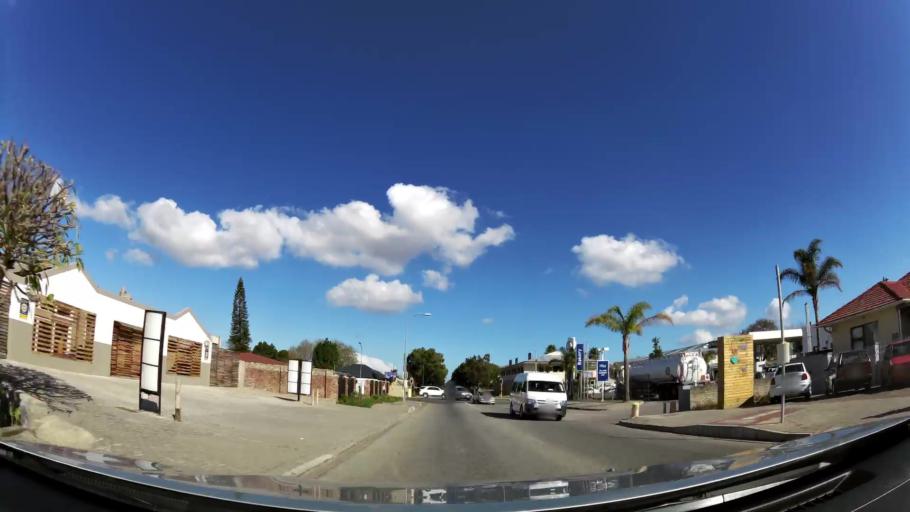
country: ZA
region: Western Cape
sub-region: Eden District Municipality
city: George
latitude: -33.9660
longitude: 22.4583
